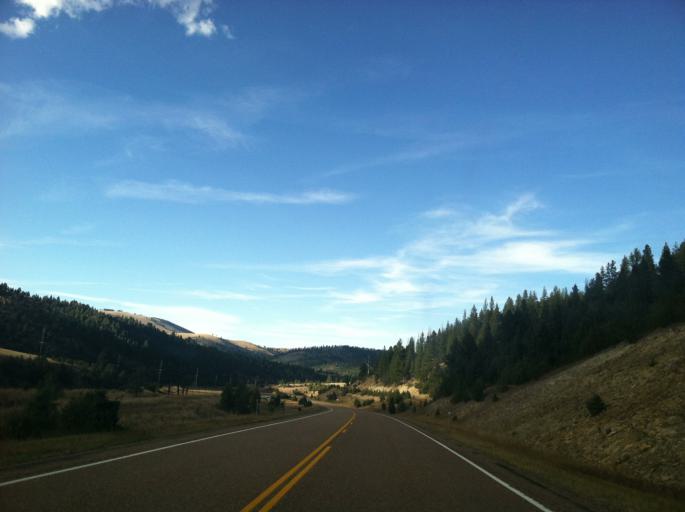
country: US
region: Montana
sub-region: Granite County
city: Philipsburg
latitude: 46.3884
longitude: -113.3091
